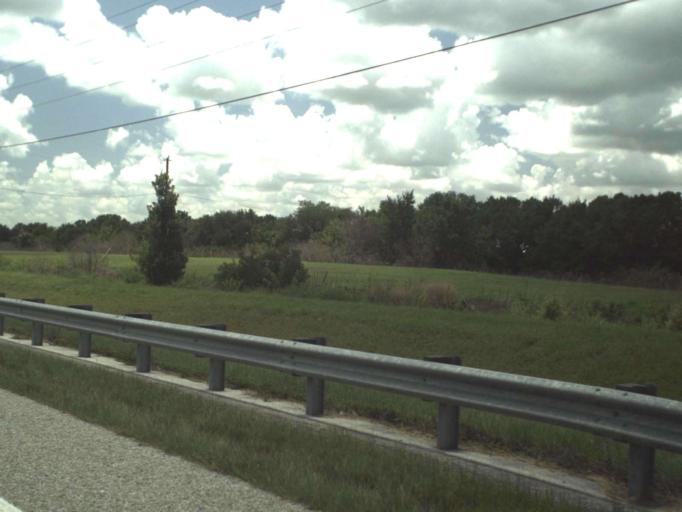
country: US
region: Florida
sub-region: Indian River County
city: Fellsmere
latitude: 27.6438
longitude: -80.7734
